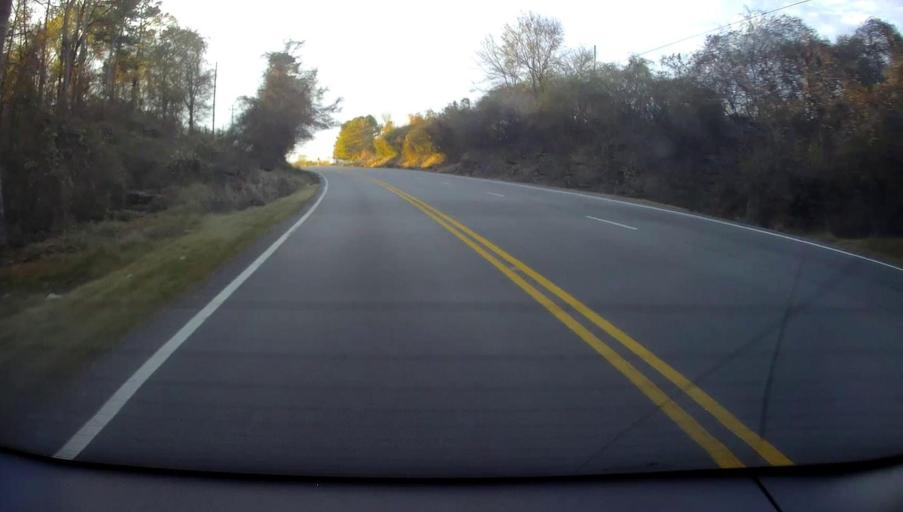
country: US
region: Alabama
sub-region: Etowah County
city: Attalla
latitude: 34.0496
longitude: -86.1791
